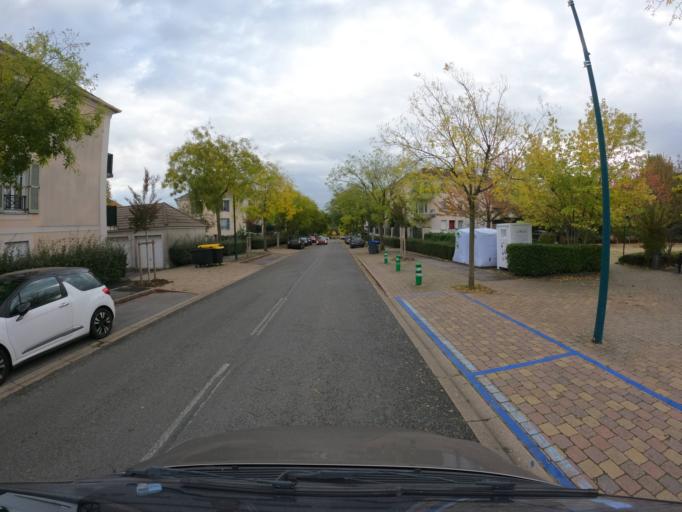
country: FR
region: Ile-de-France
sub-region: Departement de Seine-et-Marne
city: Magny-le-Hongre
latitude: 48.8666
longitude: 2.8117
